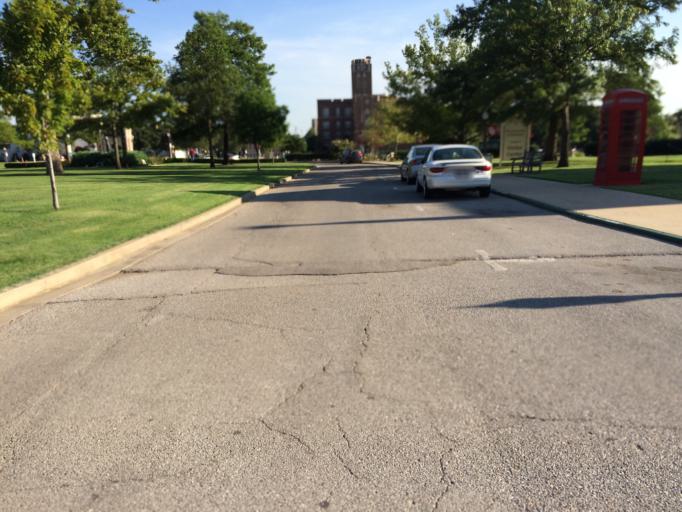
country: US
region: Oklahoma
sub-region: Cleveland County
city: Norman
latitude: 35.2101
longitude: -97.4454
